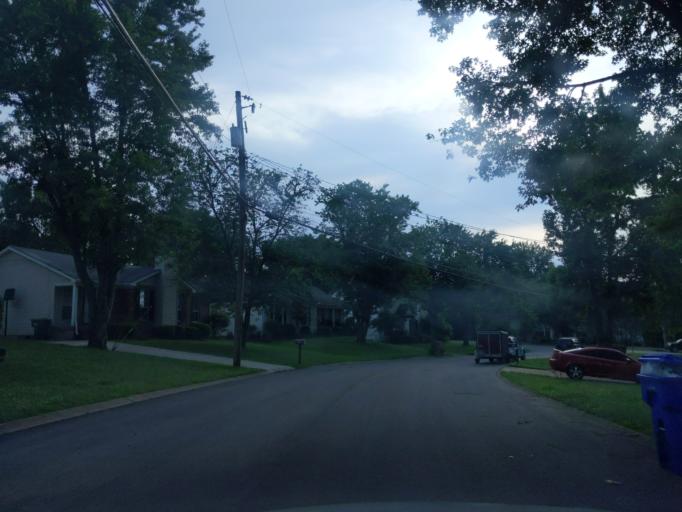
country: US
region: Tennessee
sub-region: Wilson County
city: Green Hill
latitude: 36.1869
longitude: -86.5979
